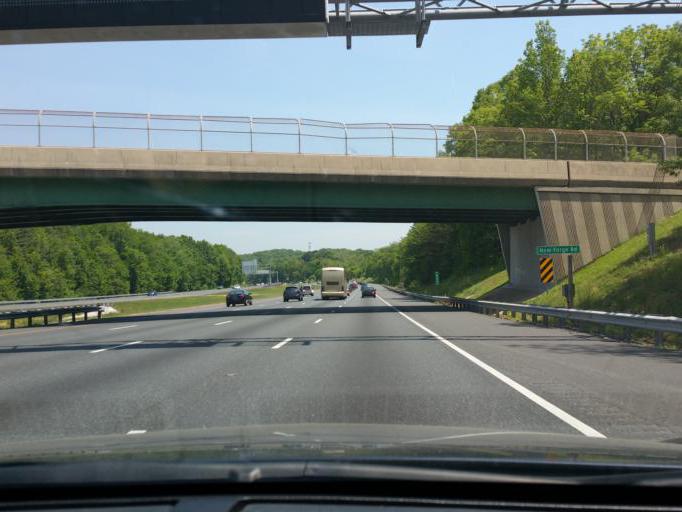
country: US
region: Maryland
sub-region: Baltimore County
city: White Marsh
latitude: 39.4084
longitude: -76.4160
